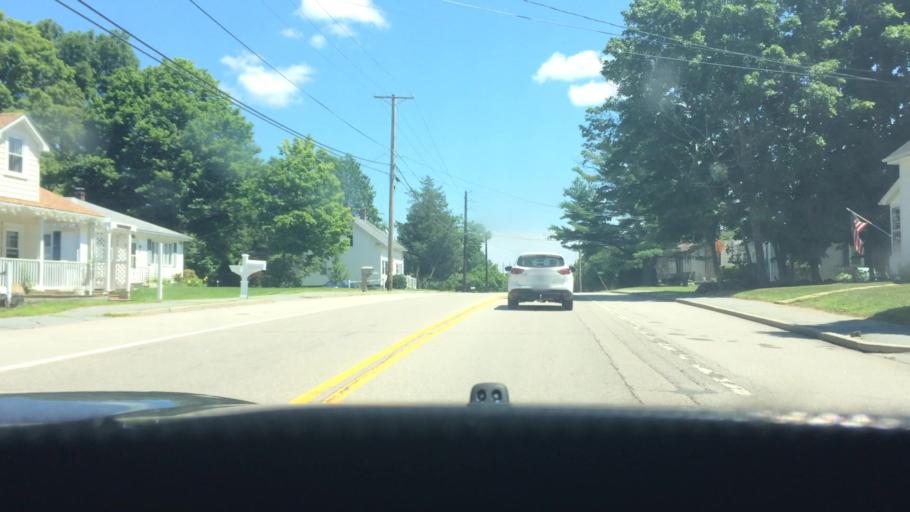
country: US
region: Massachusetts
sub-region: Worcester County
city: Blackstone
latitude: 42.0038
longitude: -71.5656
